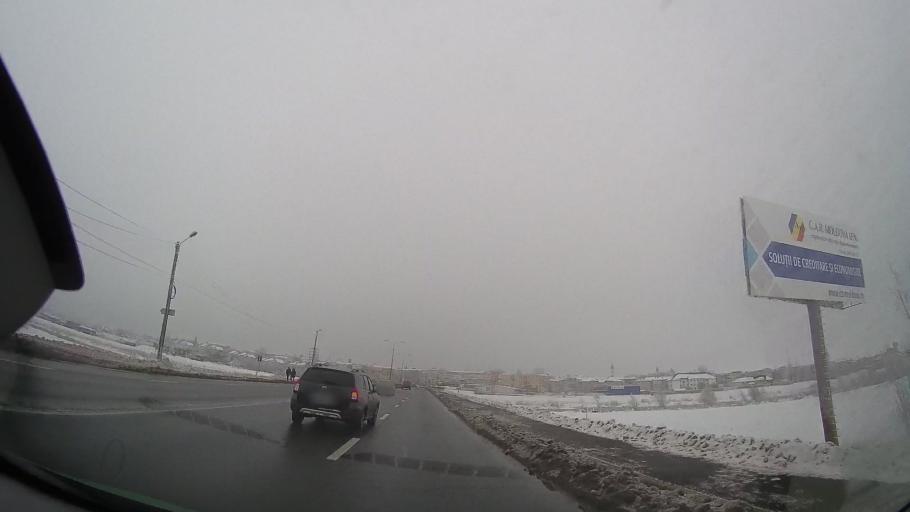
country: RO
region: Neamt
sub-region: Municipiul Roman
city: Roman
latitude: 46.9142
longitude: 26.9191
